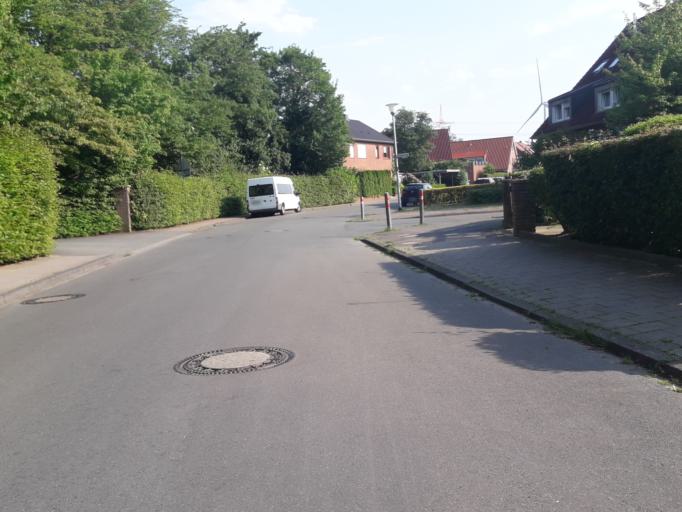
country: DE
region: North Rhine-Westphalia
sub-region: Regierungsbezirk Munster
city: Muenster
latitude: 51.8970
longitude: 7.6344
